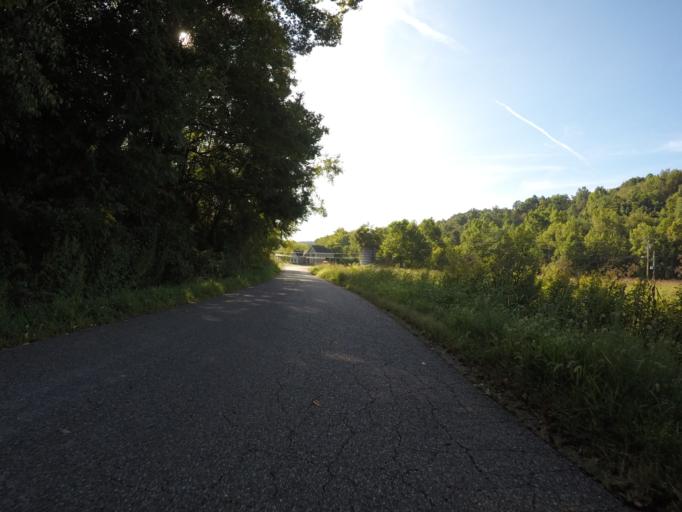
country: US
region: Ohio
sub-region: Lawrence County
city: Burlington
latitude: 38.4995
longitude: -82.5110
